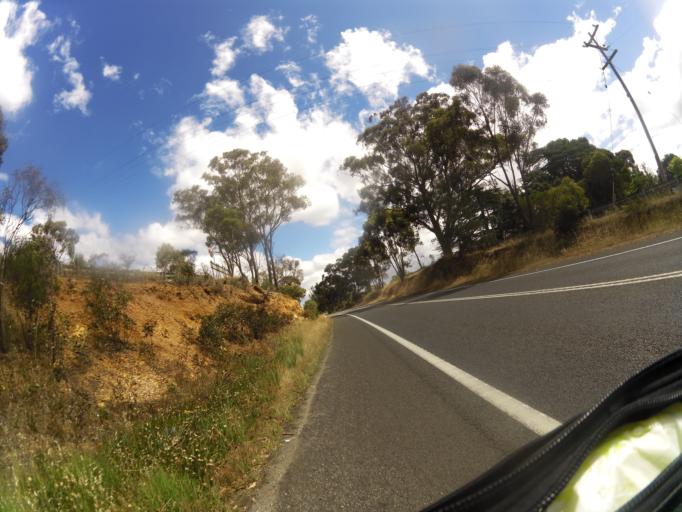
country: AU
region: Victoria
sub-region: Mount Alexander
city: Castlemaine
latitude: -37.0377
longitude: 144.2276
